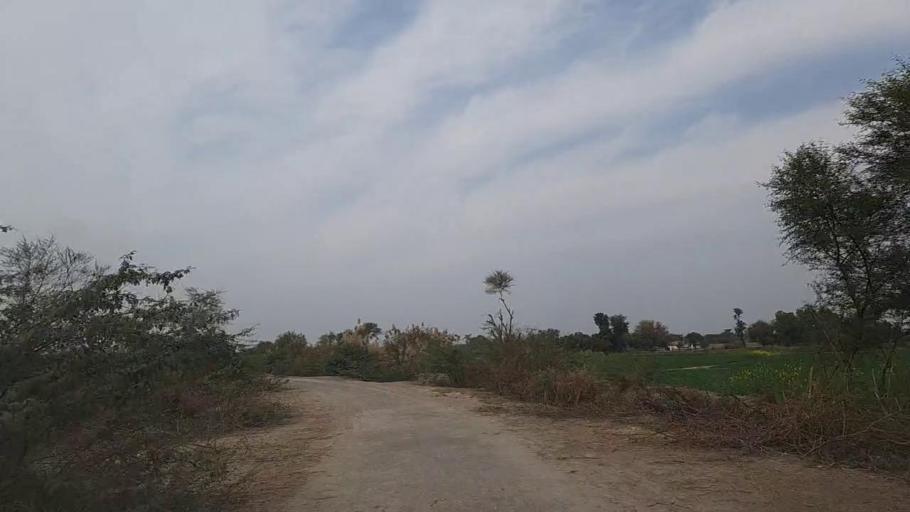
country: PK
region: Sindh
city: Daur
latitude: 26.4427
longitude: 68.4584
